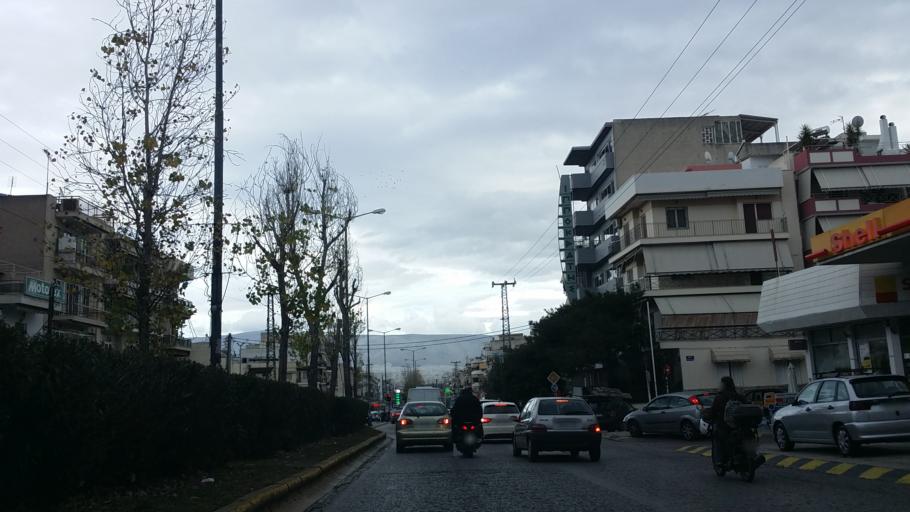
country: GR
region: Attica
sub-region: Nomarchia Athinas
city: Agia Varvara
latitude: 37.9790
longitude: 23.6595
